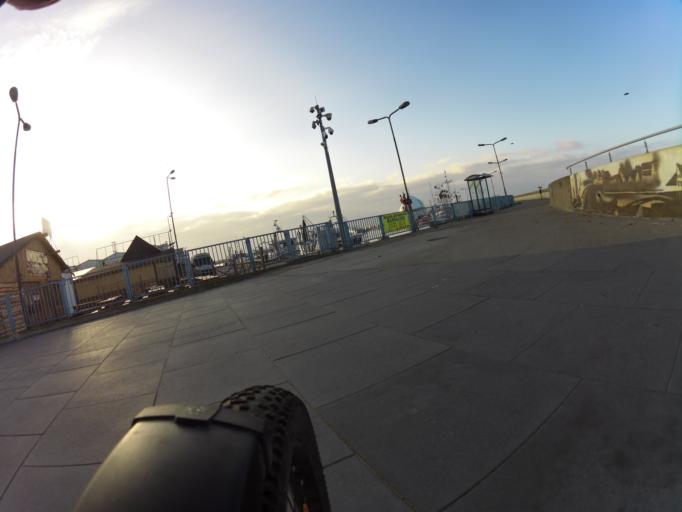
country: PL
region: Pomeranian Voivodeship
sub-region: Powiat pucki
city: Hel
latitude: 54.6048
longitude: 18.8015
